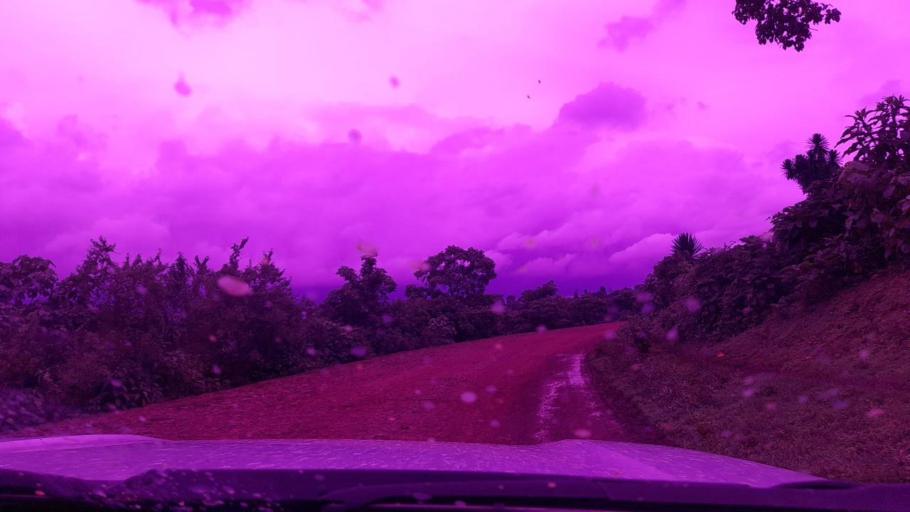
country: ET
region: Southern Nations, Nationalities, and People's Region
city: Tippi
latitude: 7.5686
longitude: 35.6616
